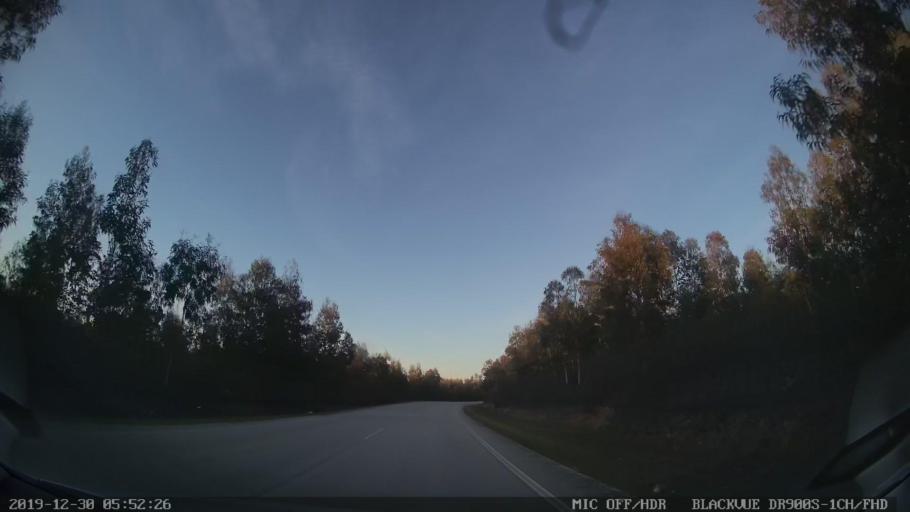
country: PT
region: Castelo Branco
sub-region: Idanha-A-Nova
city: Idanha-a-Nova
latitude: 40.0055
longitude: -7.2493
